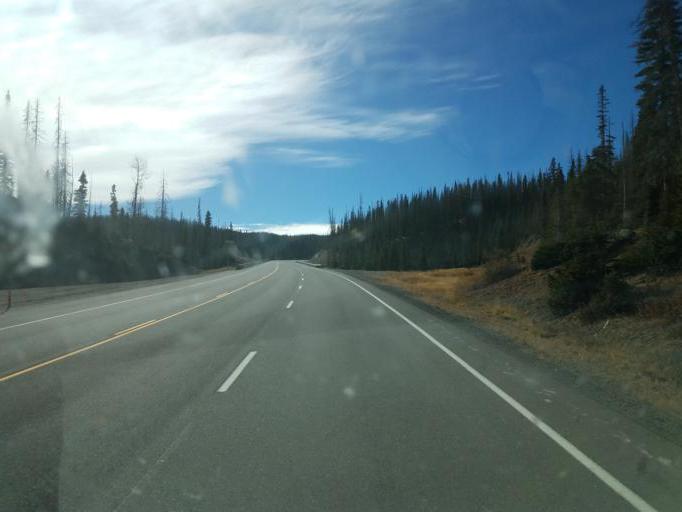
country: US
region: Colorado
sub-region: Archuleta County
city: Pagosa Springs
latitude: 37.4862
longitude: -106.7684
